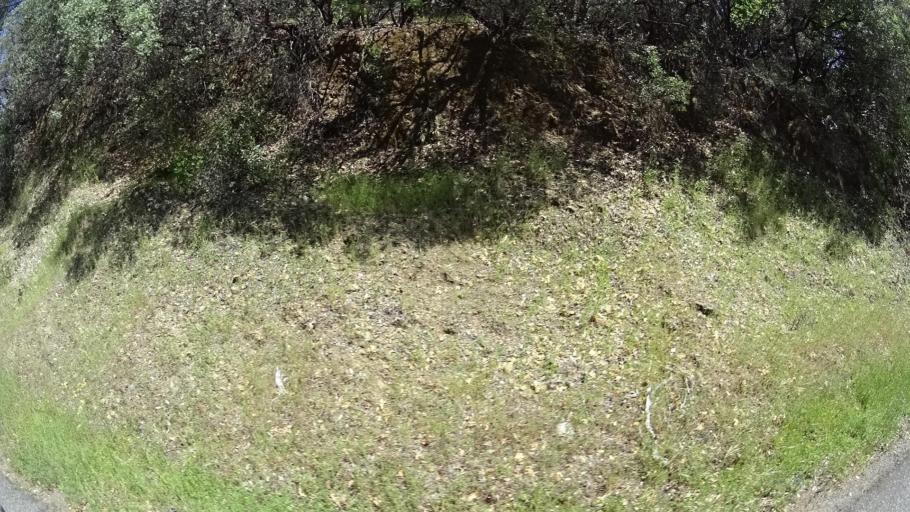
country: US
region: California
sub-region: Humboldt County
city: Redway
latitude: 40.2010
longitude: -123.5939
